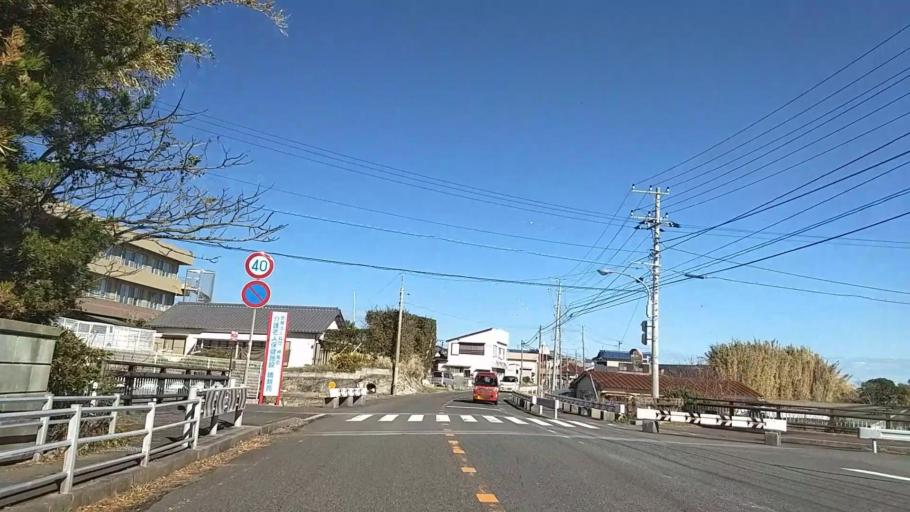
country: JP
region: Chiba
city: Tateyama
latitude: 34.9443
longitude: 139.9607
